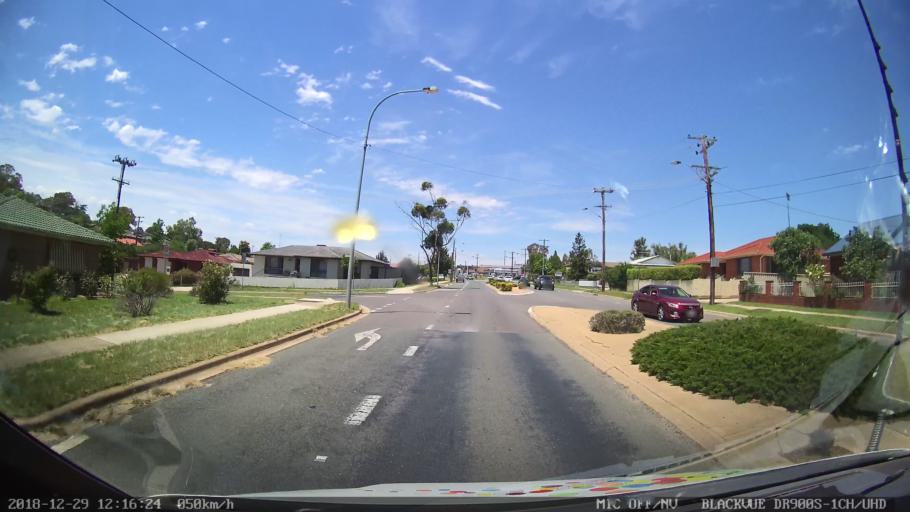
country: AU
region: New South Wales
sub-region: Queanbeyan
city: Queanbeyan
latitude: -35.3692
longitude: 149.2331
